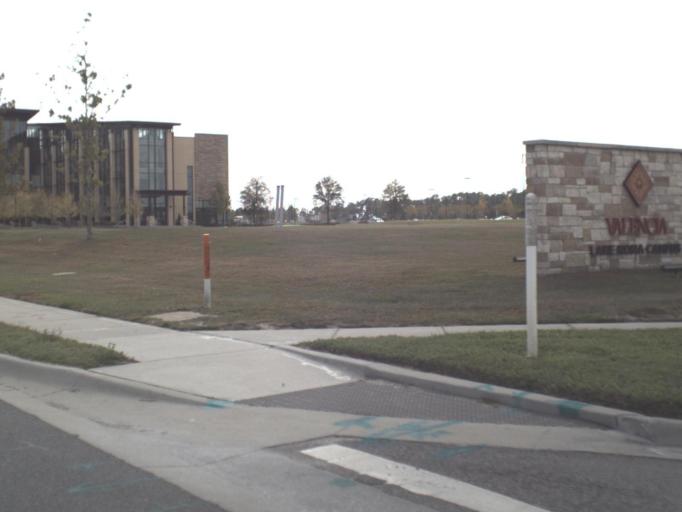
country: US
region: Florida
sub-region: Osceola County
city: Buenaventura Lakes
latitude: 28.3862
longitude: -81.2445
